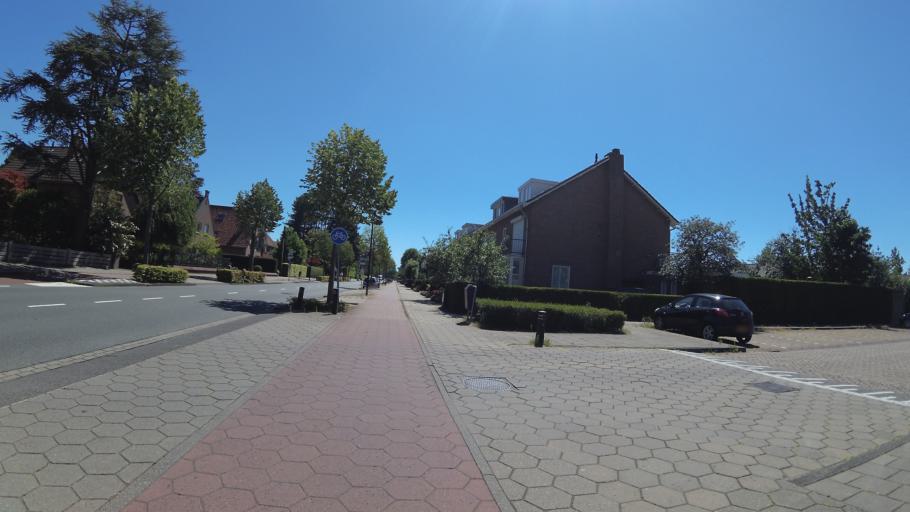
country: NL
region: North Brabant
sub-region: Gemeente Waalwijk
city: Waalwijk
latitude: 51.6835
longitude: 5.0762
